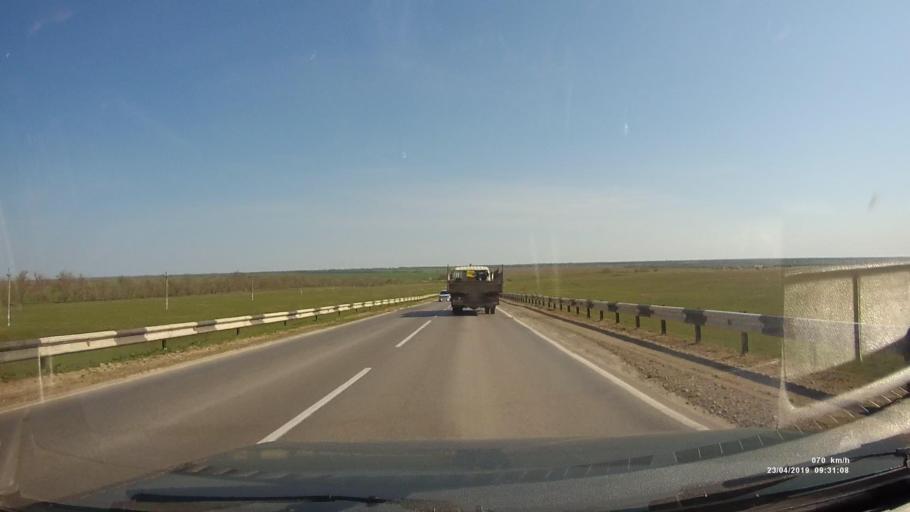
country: RU
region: Rostov
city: Gundorovskiy
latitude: 46.7771
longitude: 41.8223
